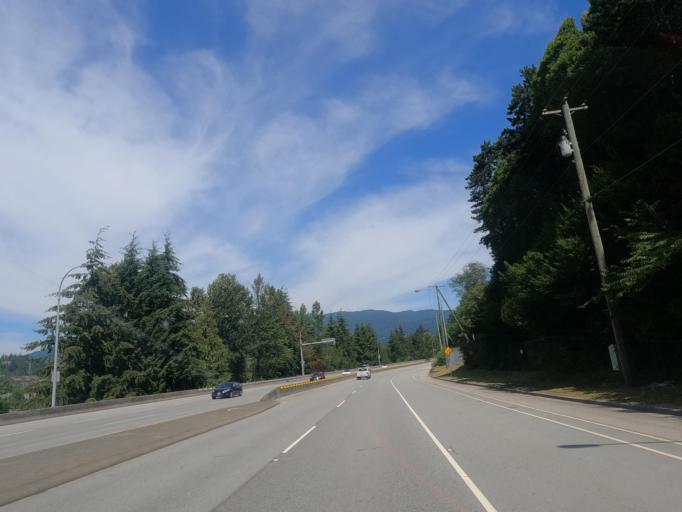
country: CA
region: British Columbia
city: Port Moody
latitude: 49.2891
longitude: -122.8962
